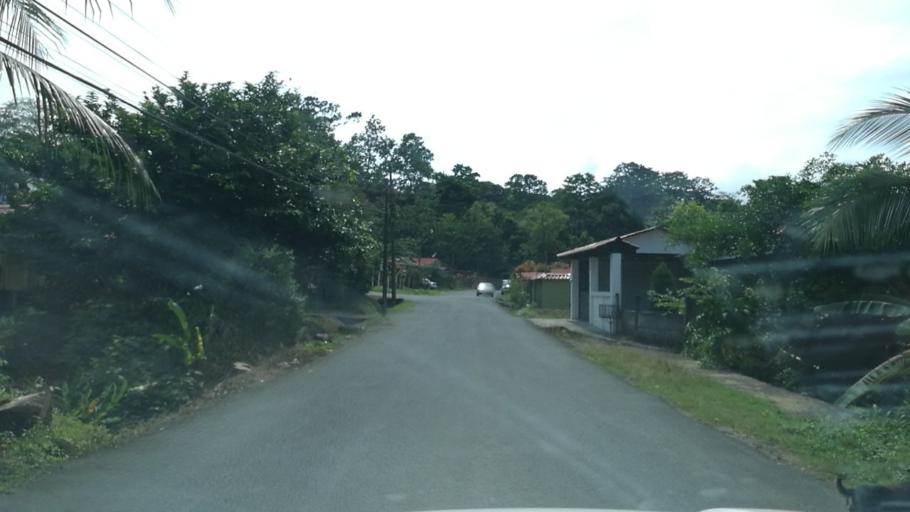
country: CR
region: Limon
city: Limon
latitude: 10.0063
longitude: -83.0570
